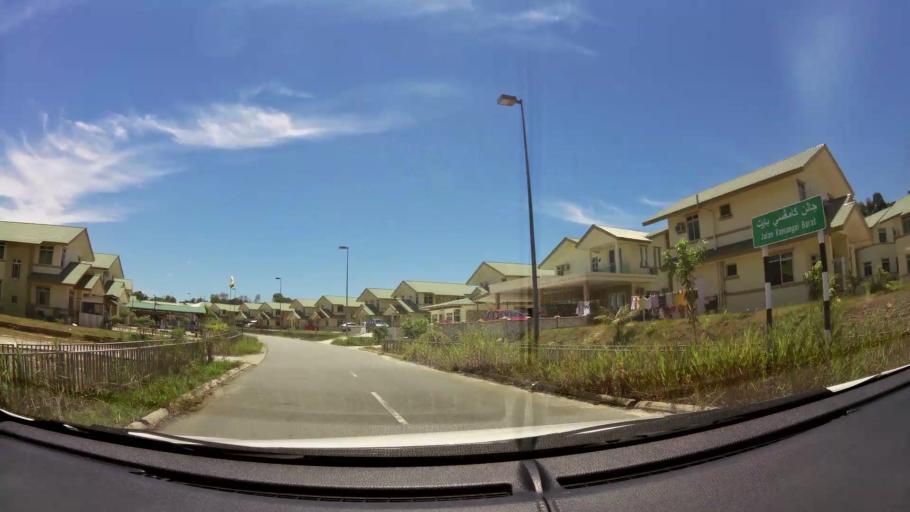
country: BN
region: Brunei and Muara
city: Bandar Seri Begawan
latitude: 5.0282
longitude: 115.0353
